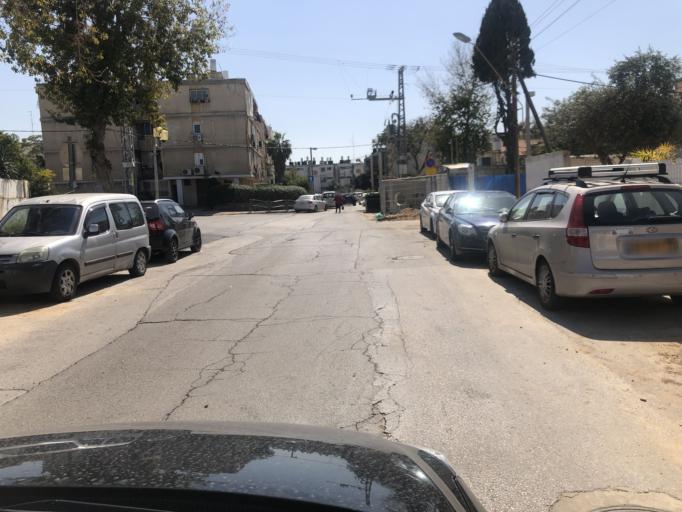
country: IL
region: Tel Aviv
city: Holon
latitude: 32.0031
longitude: 34.7627
